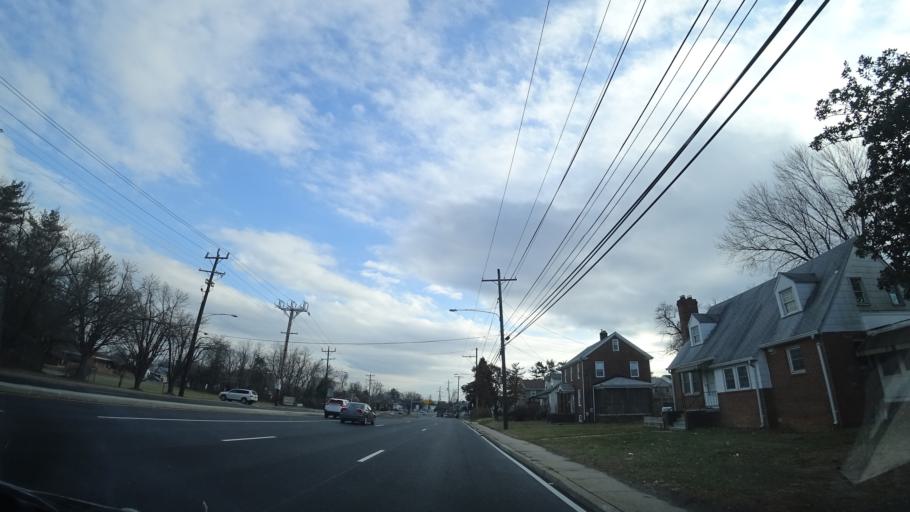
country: US
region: Maryland
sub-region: Prince George's County
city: Langley Park
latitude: 39.0045
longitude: -76.9969
